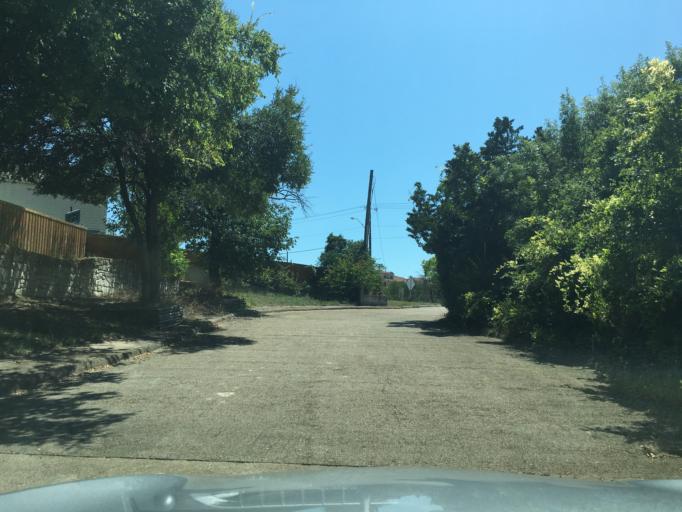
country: US
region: Texas
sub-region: Dallas County
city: Garland
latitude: 32.9521
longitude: -96.6452
